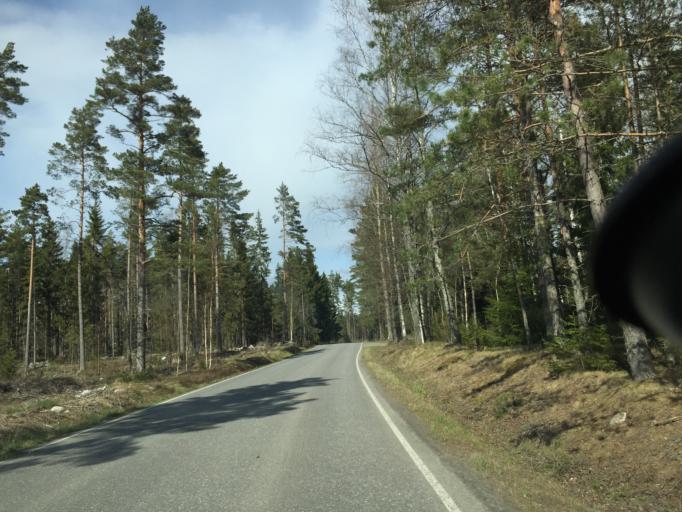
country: FI
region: Uusimaa
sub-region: Raaseporin
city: Hanko
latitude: 59.9502
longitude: 22.9579
